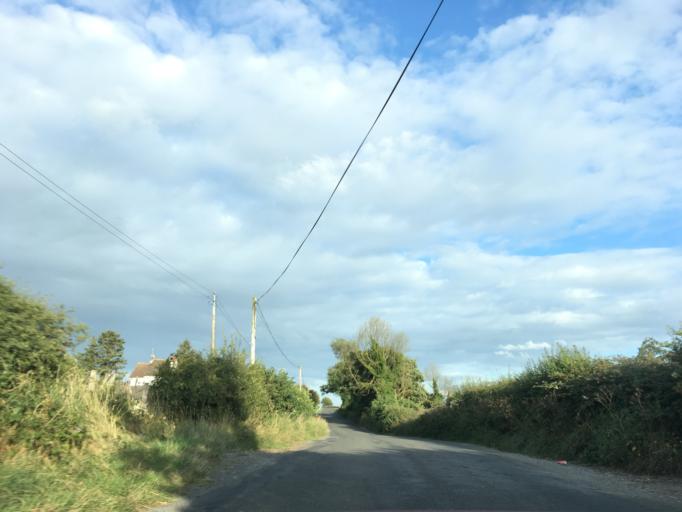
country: IE
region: Munster
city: Cashel
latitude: 52.4797
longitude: -7.9003
